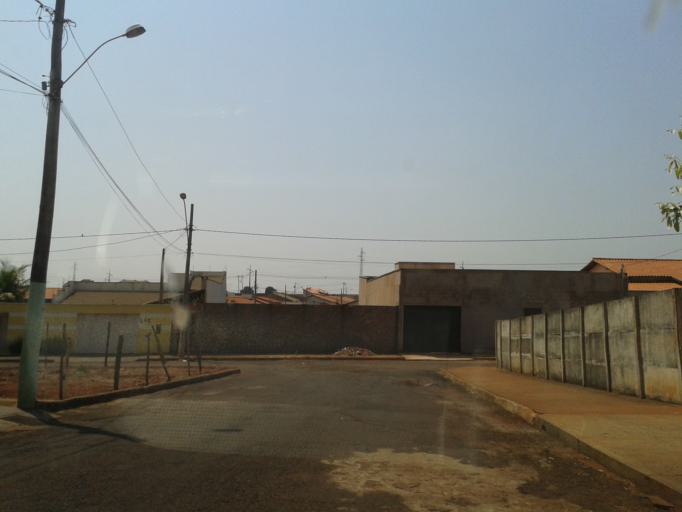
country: BR
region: Minas Gerais
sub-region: Ituiutaba
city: Ituiutaba
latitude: -18.9617
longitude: -49.4499
